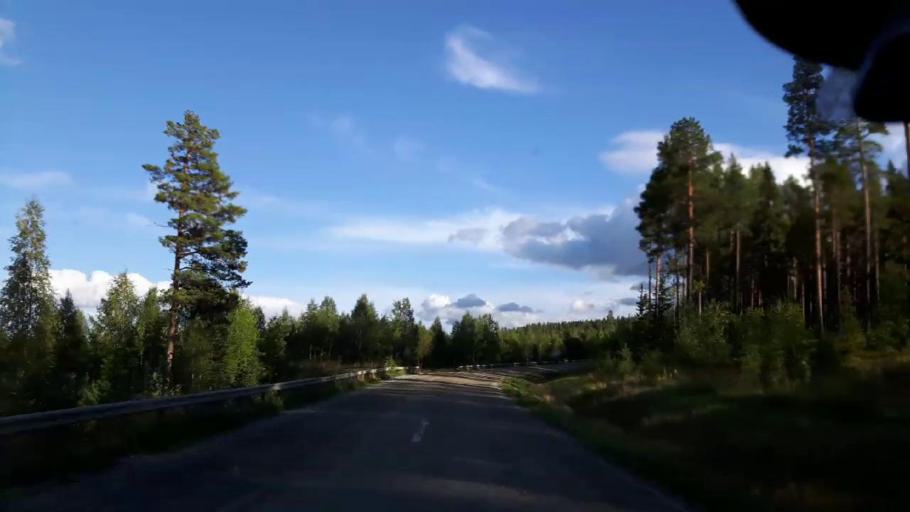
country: SE
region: Jaemtland
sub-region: Stroemsunds Kommun
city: Stroemsund
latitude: 63.3493
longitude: 15.5709
